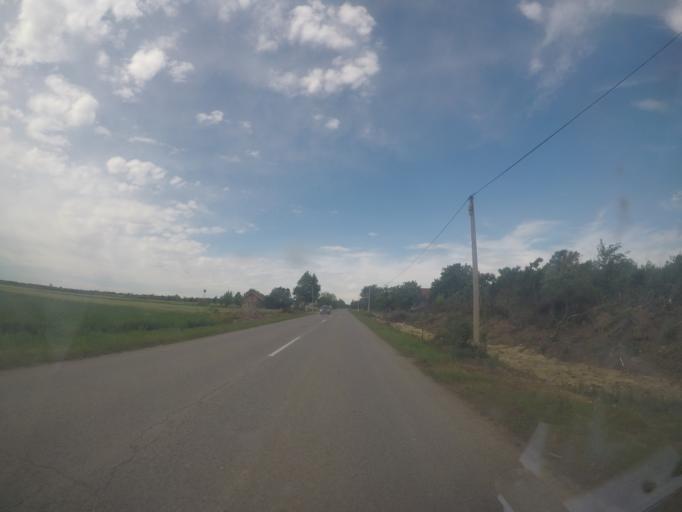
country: RS
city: Perlez
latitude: 45.2187
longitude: 20.3951
